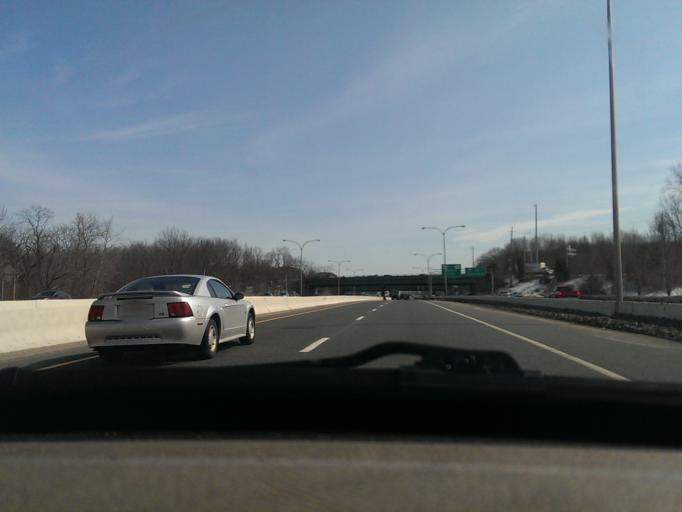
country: US
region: Rhode Island
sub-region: Providence County
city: Cumberland Hill
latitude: 41.9454
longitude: -71.4790
